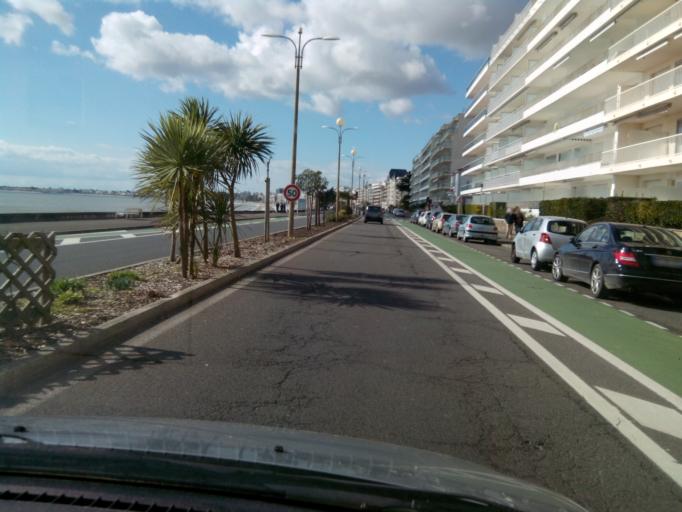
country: FR
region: Pays de la Loire
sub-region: Departement de la Loire-Atlantique
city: La Baule-Escoublac
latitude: 47.2800
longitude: -2.3796
